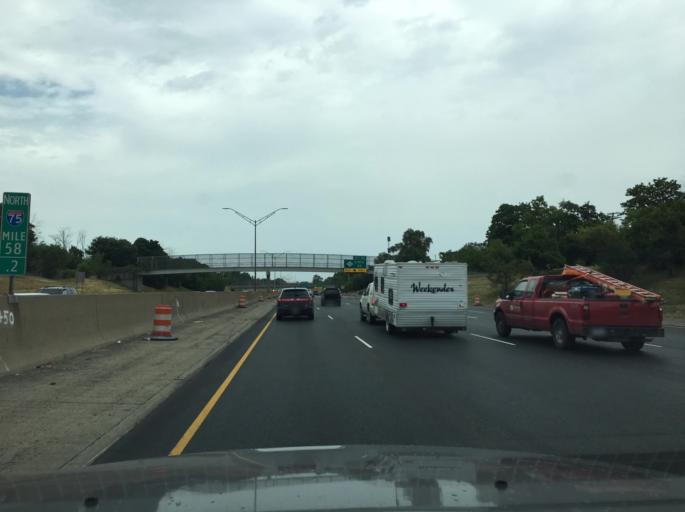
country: US
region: Michigan
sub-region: Oakland County
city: Hazel Park
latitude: 42.4364
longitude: -83.0949
